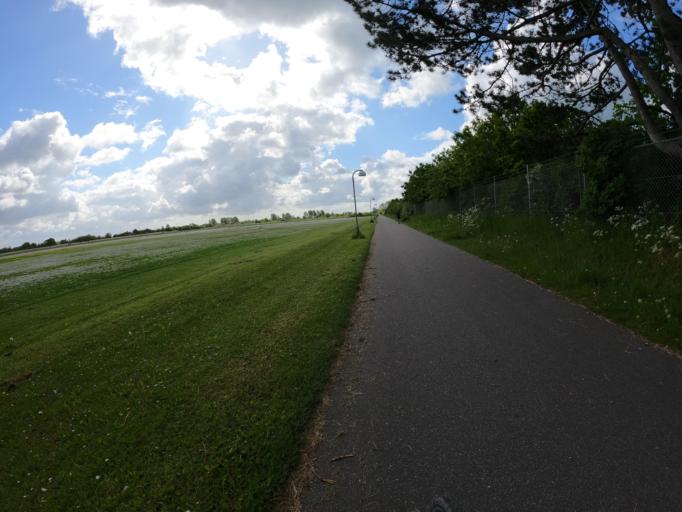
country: DK
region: Capital Region
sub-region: Ishoj Kommune
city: Ishoj
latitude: 55.6124
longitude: 12.3728
